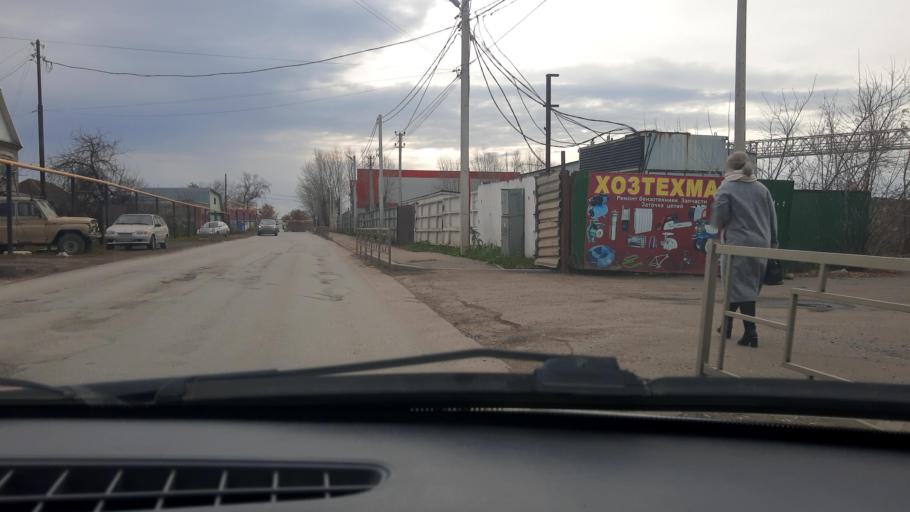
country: RU
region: Bashkortostan
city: Mikhaylovka
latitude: 54.6987
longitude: 55.8492
